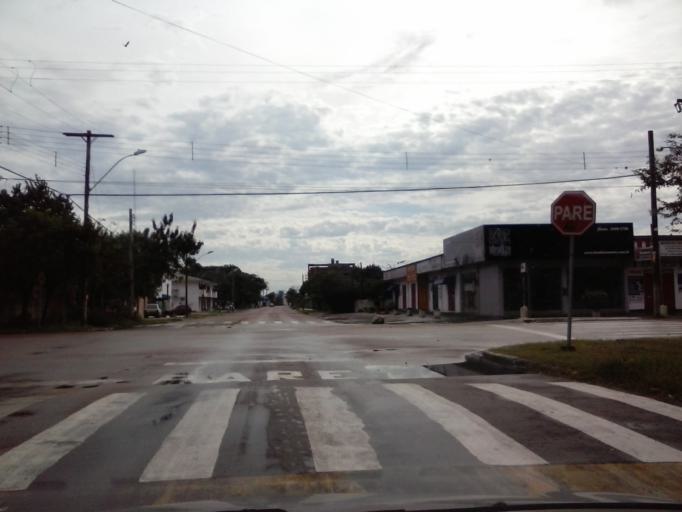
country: BR
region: Rio Grande do Sul
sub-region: Porto Alegre
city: Porto Alegre
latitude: -30.0004
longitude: -51.3081
